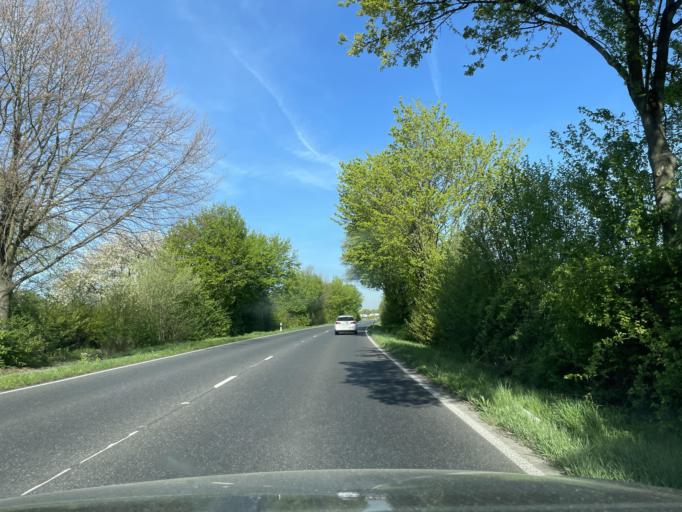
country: DE
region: North Rhine-Westphalia
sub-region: Regierungsbezirk Dusseldorf
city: Juchen
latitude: 51.1137
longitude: 6.4438
